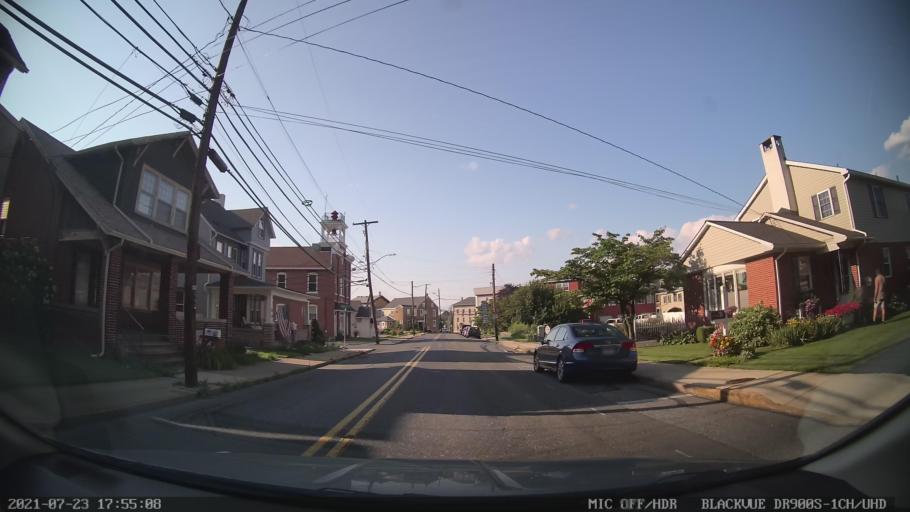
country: US
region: Pennsylvania
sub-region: Lehigh County
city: Macungie
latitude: 40.5146
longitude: -75.5556
